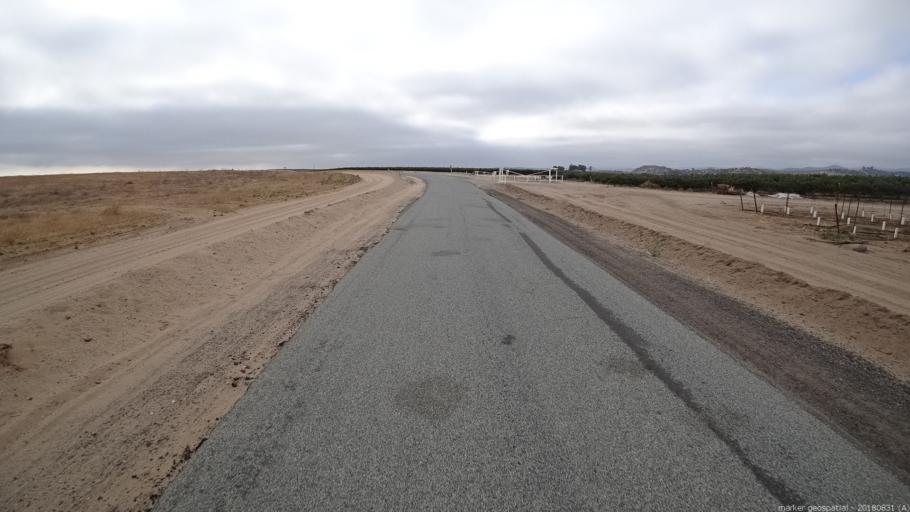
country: US
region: California
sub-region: Monterey County
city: King City
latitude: 36.1548
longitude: -121.1048
